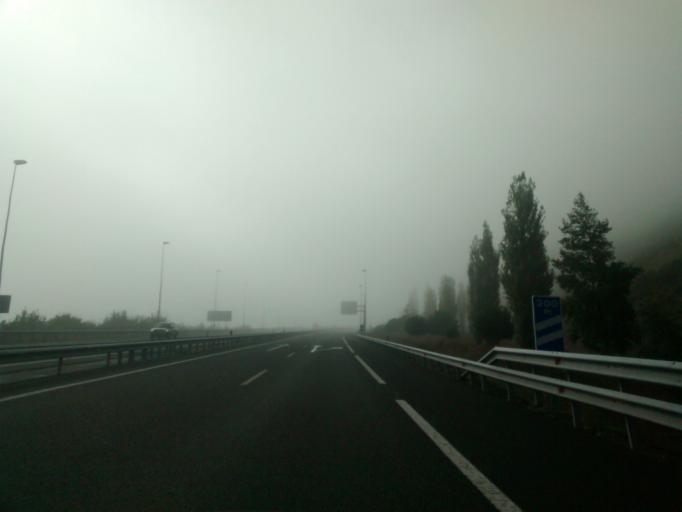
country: ES
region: Cantabria
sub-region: Provincia de Cantabria
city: Arenas de Iguna
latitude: 43.1719
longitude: -4.0535
